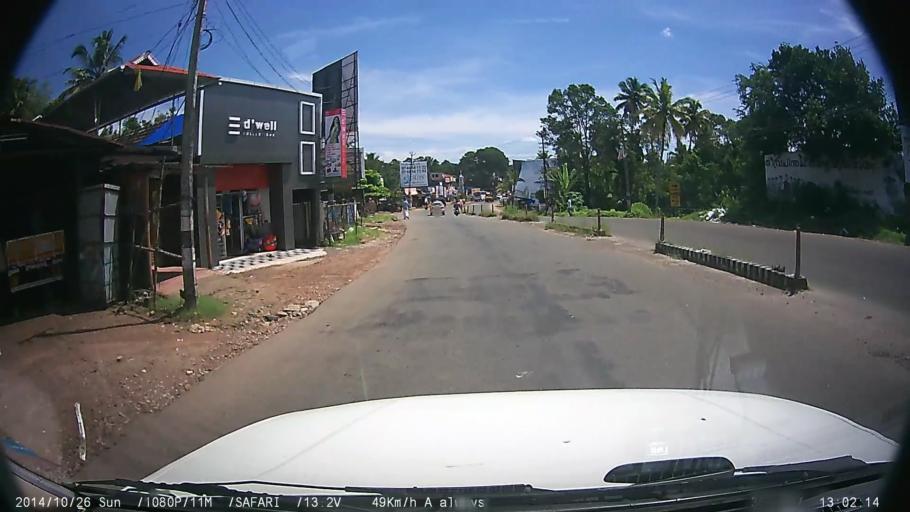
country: IN
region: Kerala
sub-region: Kottayam
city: Changanacheri
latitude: 9.5018
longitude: 76.5244
